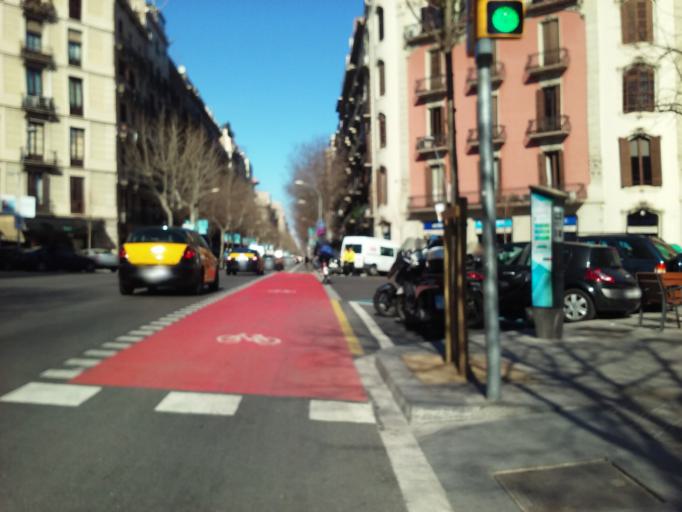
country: ES
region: Catalonia
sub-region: Provincia de Barcelona
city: Eixample
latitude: 41.3887
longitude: 2.1624
